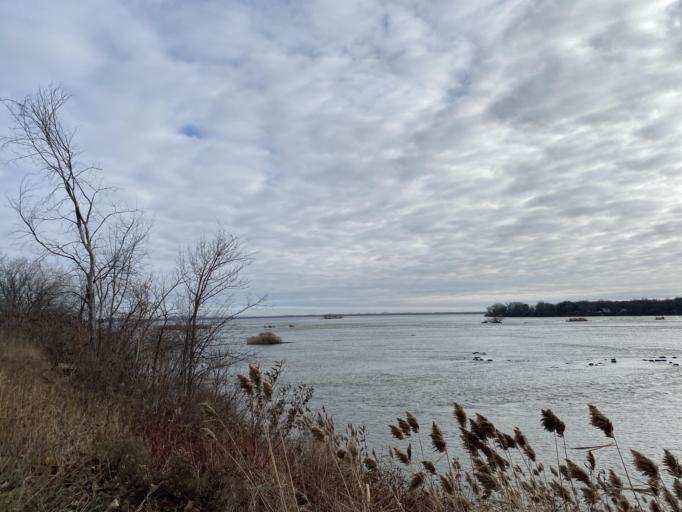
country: CA
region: Quebec
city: Saint-Raymond
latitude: 45.4320
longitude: -73.5891
